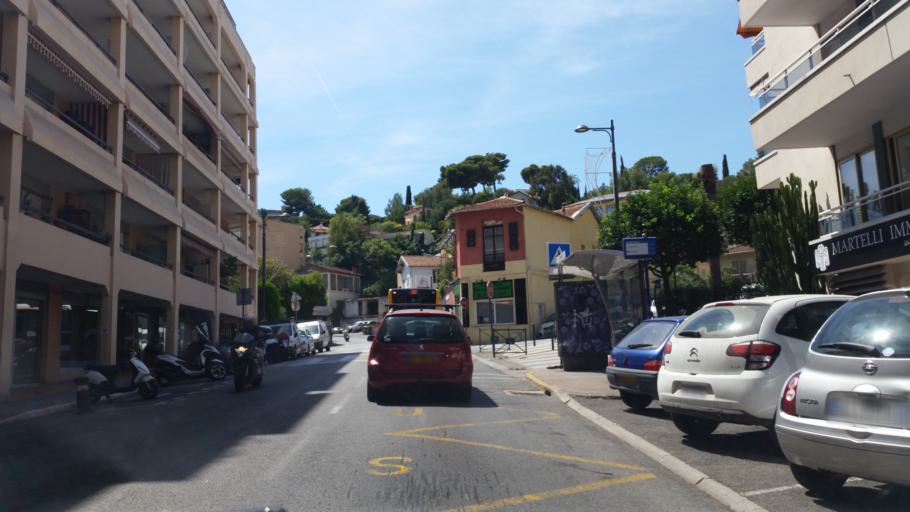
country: FR
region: Provence-Alpes-Cote d'Azur
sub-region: Departement des Alpes-Maritimes
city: Roquebrune-Cap-Martin
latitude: 43.7631
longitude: 7.4793
